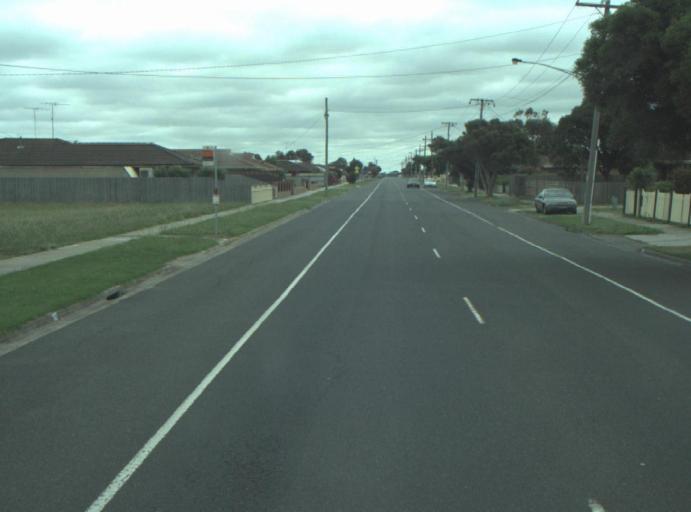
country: AU
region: Victoria
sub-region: Greater Geelong
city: Bell Post Hill
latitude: -38.0718
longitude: 144.3486
